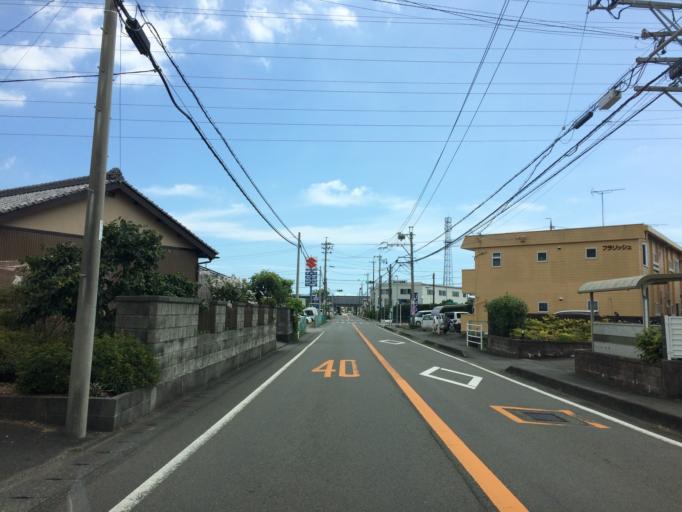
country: JP
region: Shizuoka
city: Yaizu
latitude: 34.8903
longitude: 138.3107
